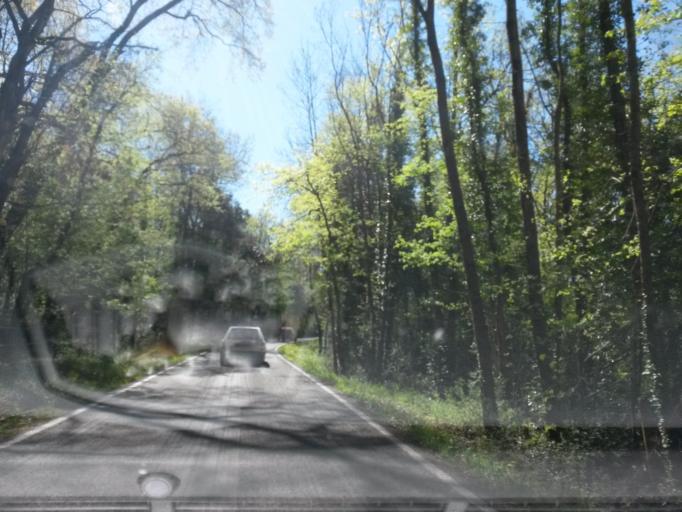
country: ES
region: Catalonia
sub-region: Provincia de Girona
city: Sant Cristofol de les Fonts
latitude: 42.1747
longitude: 2.5081
